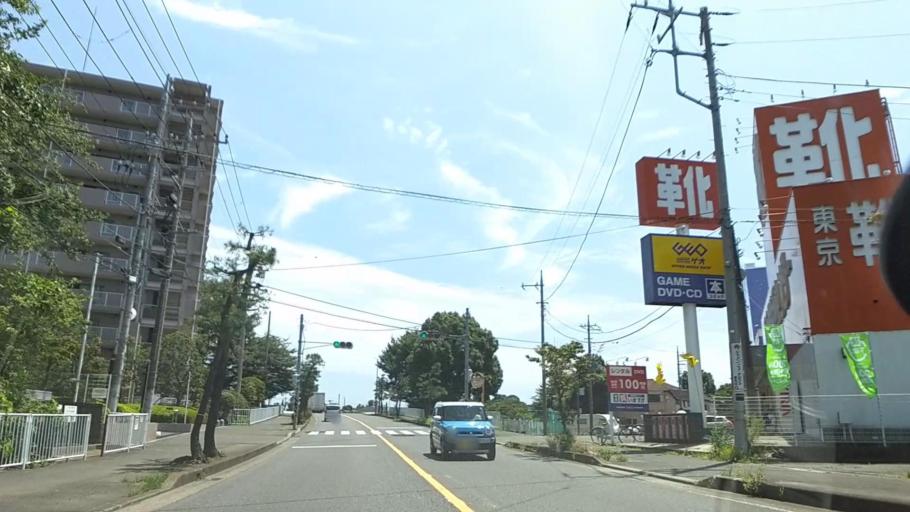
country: JP
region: Kanagawa
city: Atsugi
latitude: 35.3841
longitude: 139.3822
